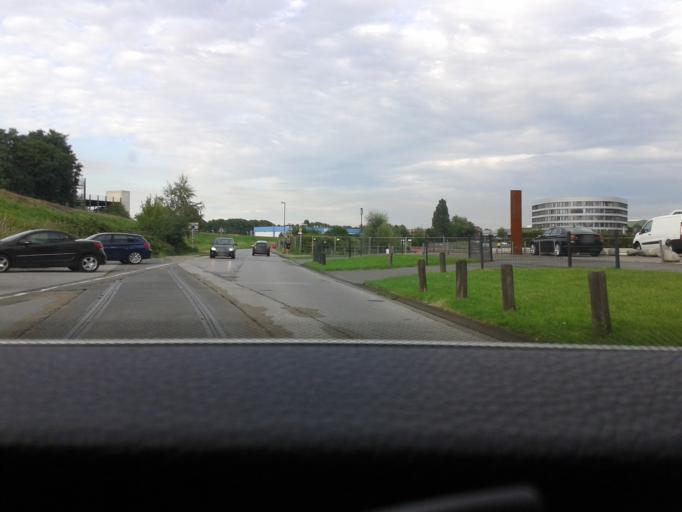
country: DE
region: North Rhine-Westphalia
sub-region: Regierungsbezirk Dusseldorf
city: Duisburg
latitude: 51.4404
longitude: 6.7643
